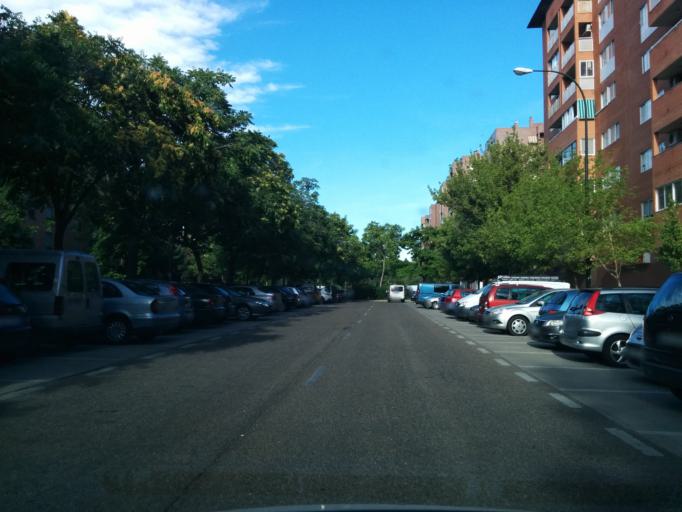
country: ES
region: Aragon
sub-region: Provincia de Zaragoza
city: Zaragoza
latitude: 41.6689
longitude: -0.8860
